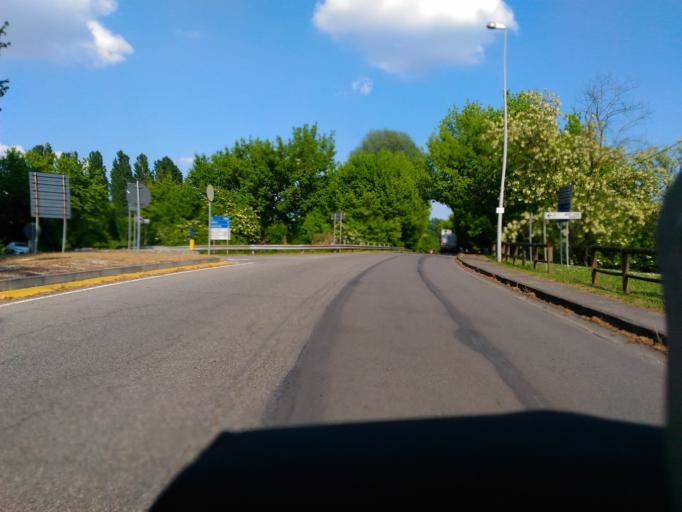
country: IT
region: Lombardy
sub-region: Citta metropolitana di Milano
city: Tribiano
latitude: 45.4024
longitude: 9.3604
